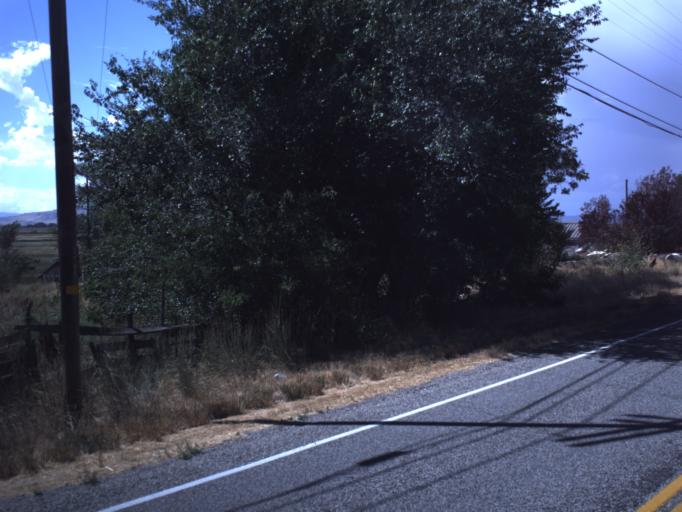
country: US
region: Utah
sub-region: Box Elder County
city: Brigham City
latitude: 41.5782
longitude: -112.0336
